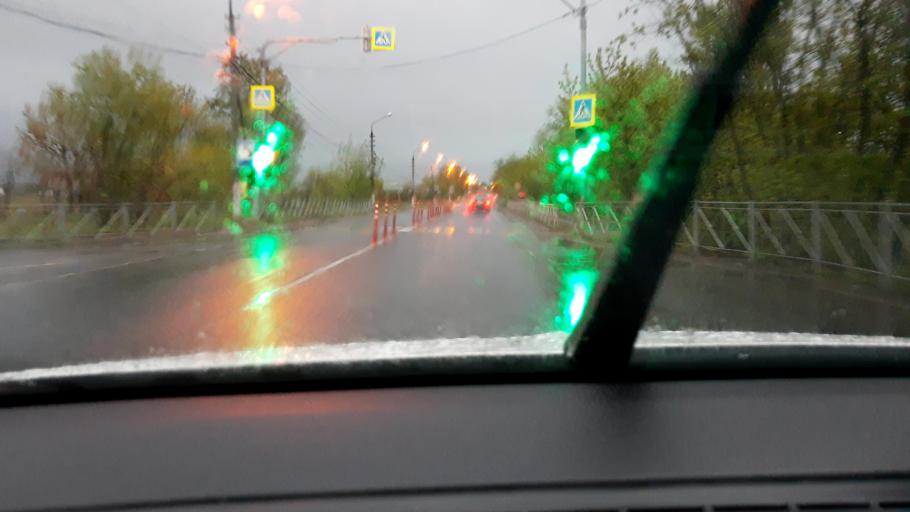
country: RU
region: Moskovskaya
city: Zagoryanskiy
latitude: 55.9287
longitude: 37.9395
